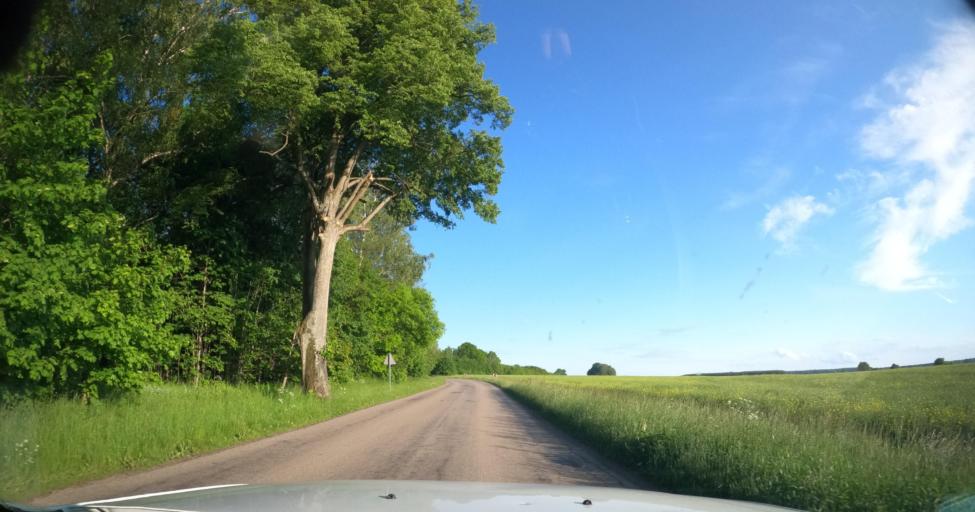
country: PL
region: Warmian-Masurian Voivodeship
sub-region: Powiat braniewski
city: Braniewo
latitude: 54.2831
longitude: 19.8955
